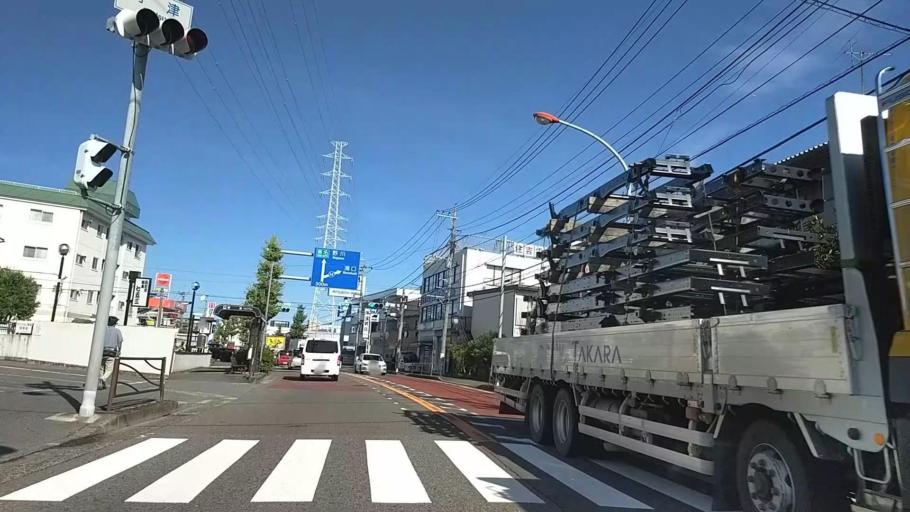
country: JP
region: Kanagawa
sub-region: Kawasaki-shi
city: Kawasaki
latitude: 35.5690
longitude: 139.6363
